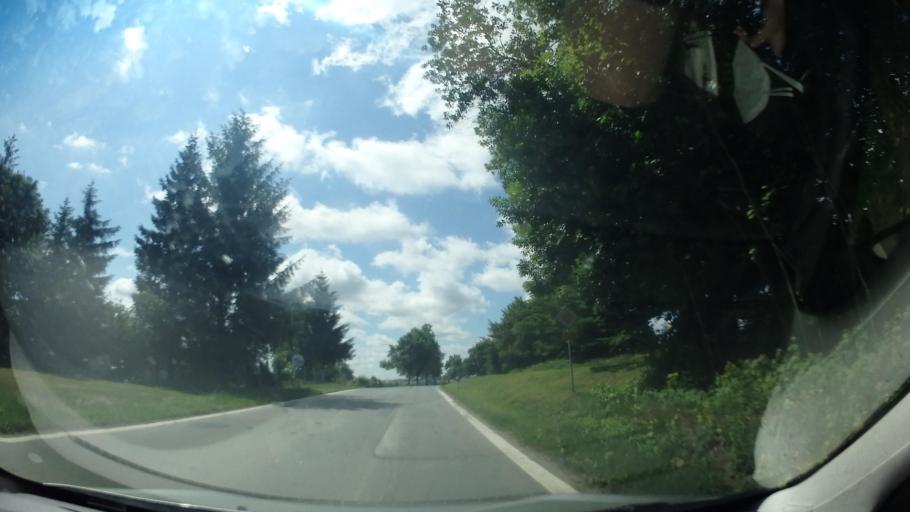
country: CZ
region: Vysocina
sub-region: Okres Zd'ar nad Sazavou
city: Zd'ar nad Sazavou
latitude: 49.5807
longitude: 15.9652
